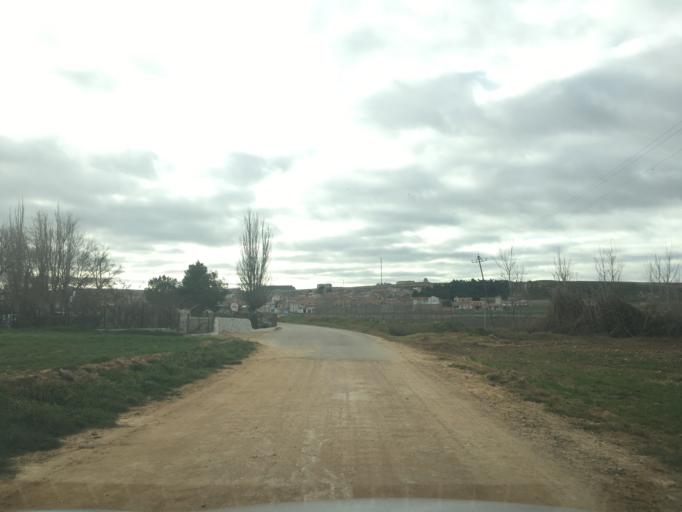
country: ES
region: Castille-La Mancha
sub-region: Provincia de Albacete
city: Petrola
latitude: 38.8325
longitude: -1.5581
